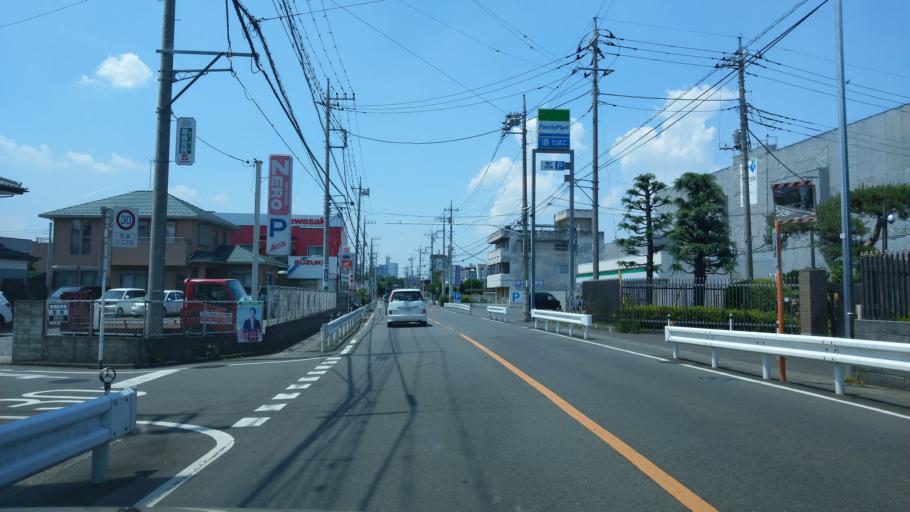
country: JP
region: Saitama
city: Yono
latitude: 35.8715
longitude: 139.6624
